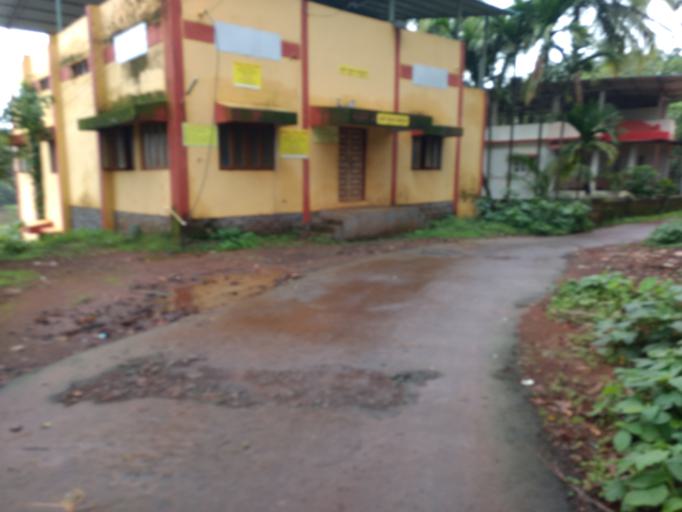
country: IN
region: Maharashtra
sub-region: Ratnagiri
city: Guhagar
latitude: 17.4952
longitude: 73.1886
